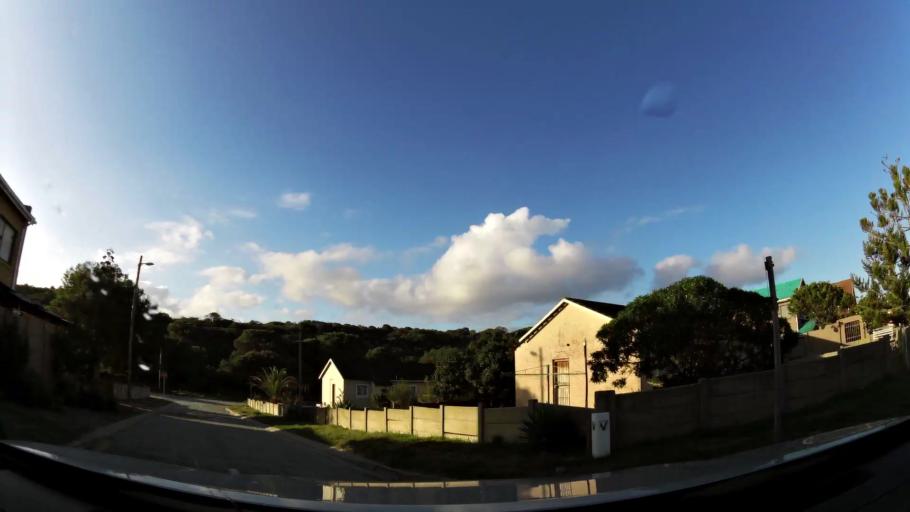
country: ZA
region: Western Cape
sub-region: Eden District Municipality
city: George
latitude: -34.0024
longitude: 22.6568
